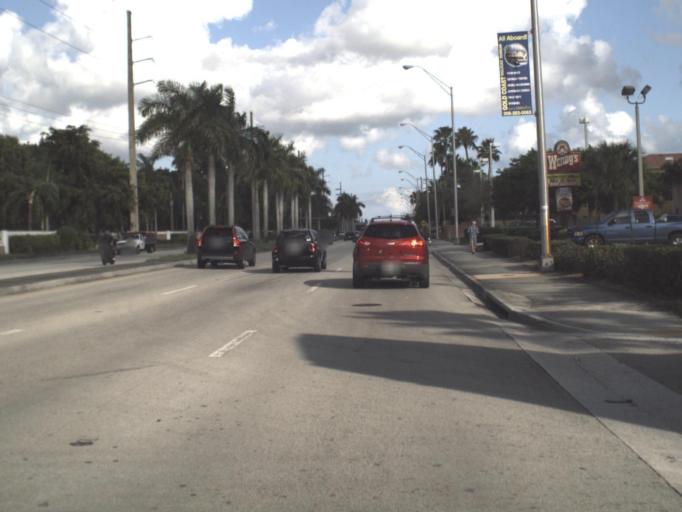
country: US
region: Florida
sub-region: Miami-Dade County
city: Country Walk
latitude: 25.6262
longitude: -80.4127
